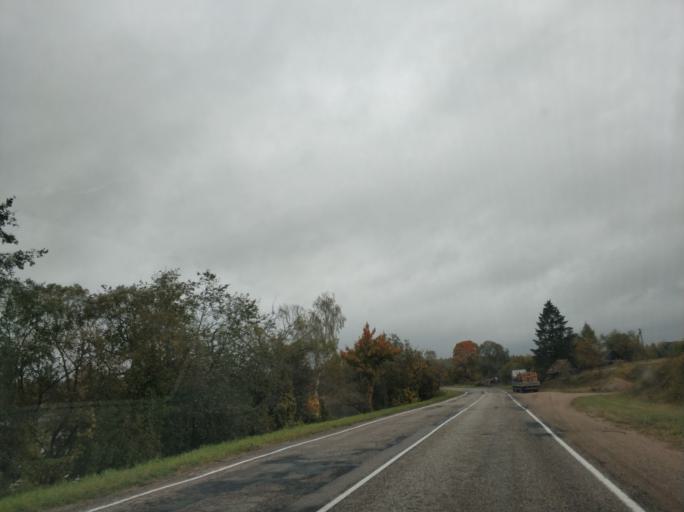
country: RU
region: Pskov
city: Sebezh
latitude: 56.2898
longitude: 28.5845
